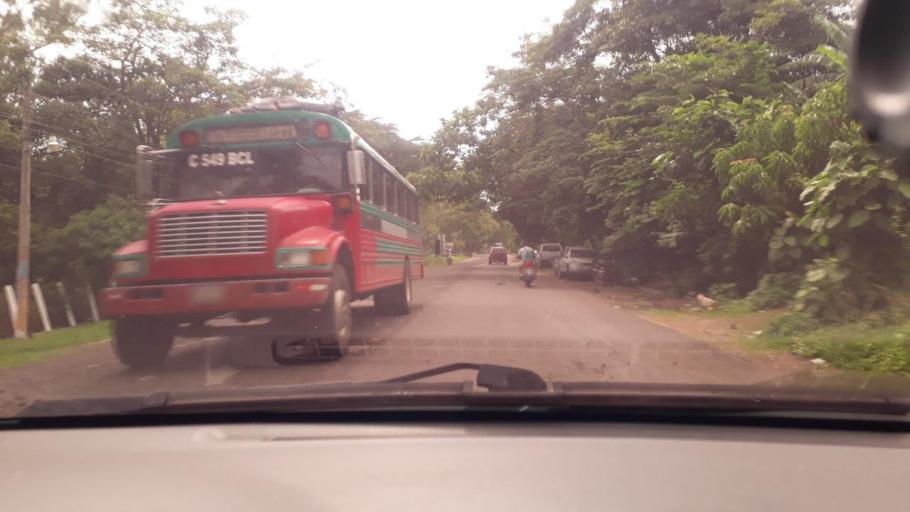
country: GT
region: Jutiapa
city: Jalpatagua
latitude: 14.1417
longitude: -90.0222
